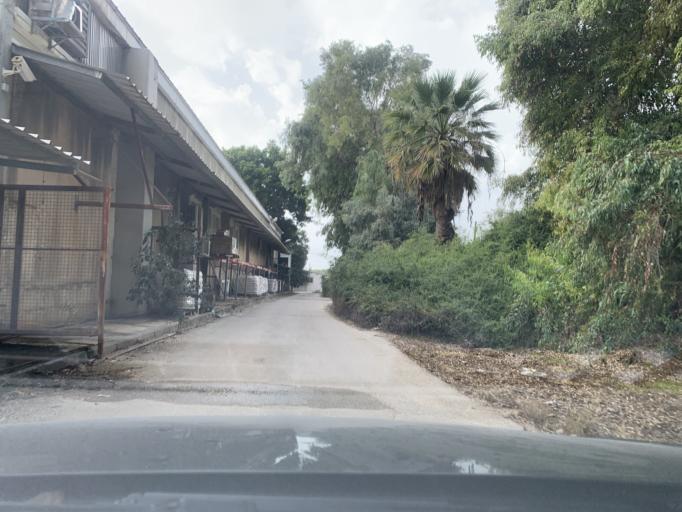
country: IL
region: Central District
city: Tirah
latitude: 32.2200
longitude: 34.9379
